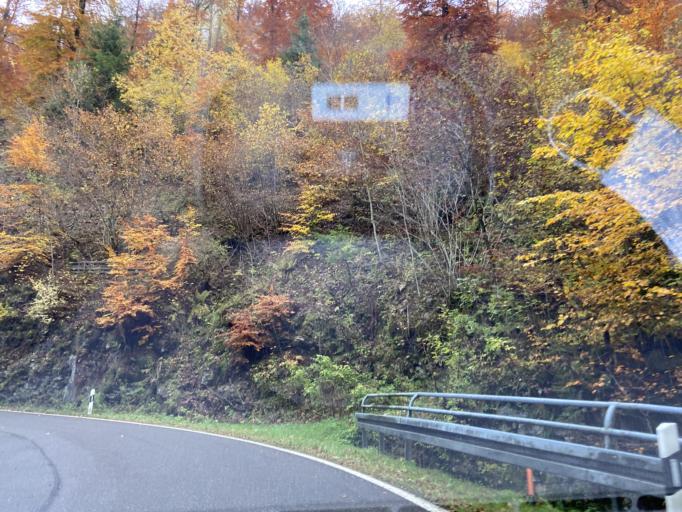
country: DE
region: Baden-Wuerttemberg
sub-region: Tuebingen Region
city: Leibertingen
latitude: 48.0692
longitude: 9.0346
